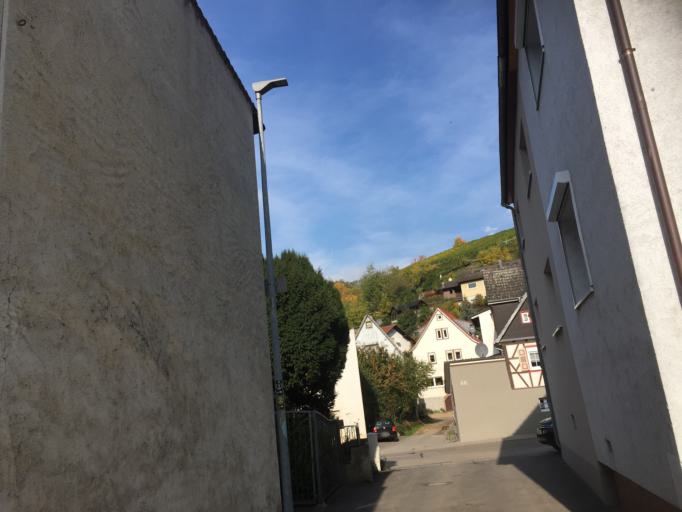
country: DE
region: Hesse
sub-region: Regierungsbezirk Darmstadt
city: Bensheim
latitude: 49.6752
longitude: 8.6400
